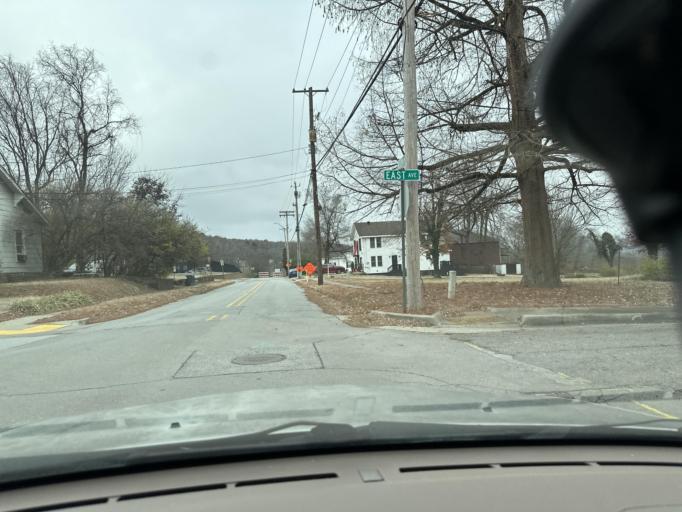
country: US
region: Arkansas
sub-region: Washington County
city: Fayetteville
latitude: 36.0609
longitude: -94.1598
